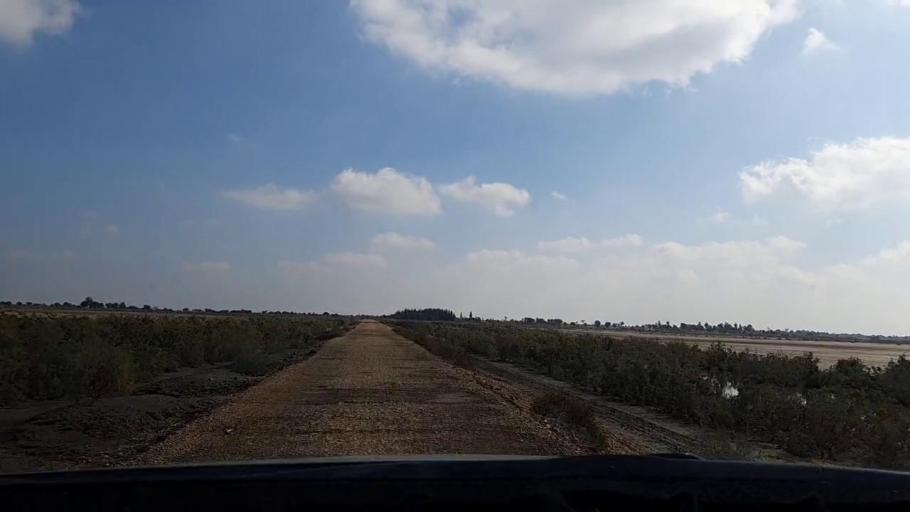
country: PK
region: Sindh
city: Pithoro
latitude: 25.7337
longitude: 69.2819
